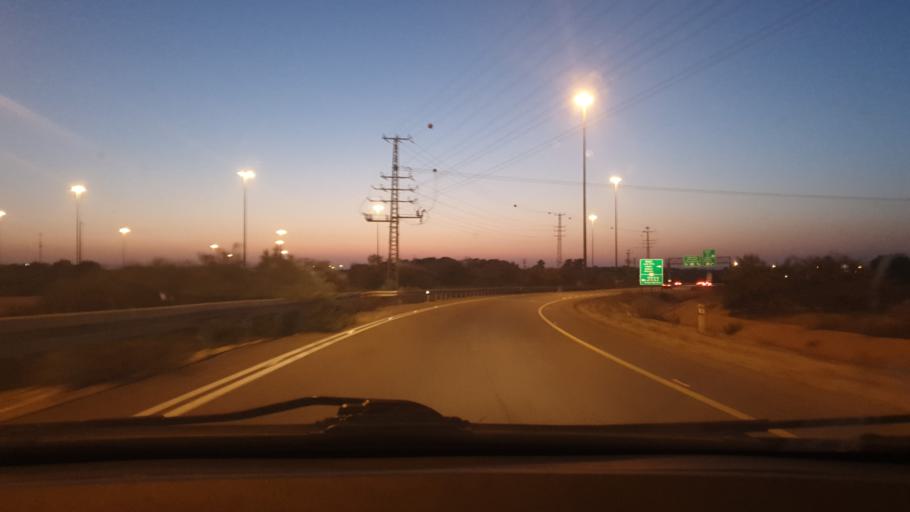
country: IL
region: Central District
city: Gedera
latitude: 31.8035
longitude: 34.7684
